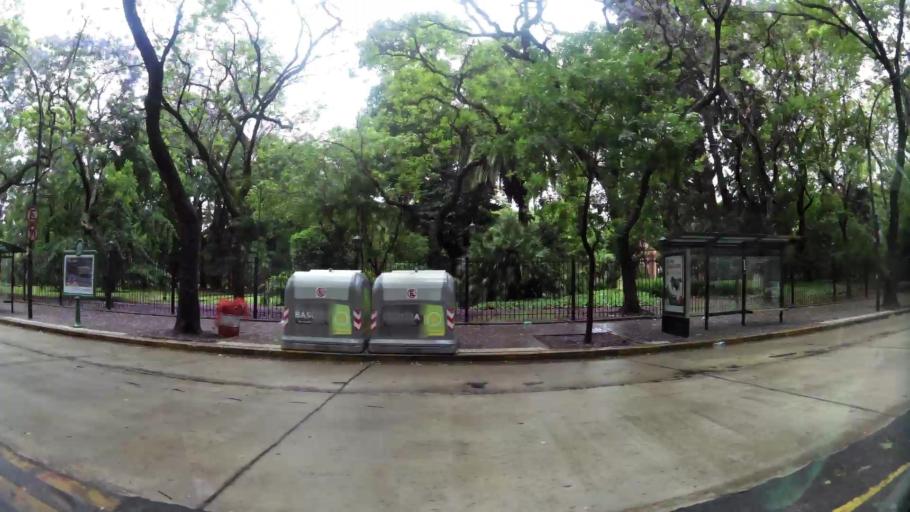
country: AR
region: Buenos Aires F.D.
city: Colegiales
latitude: -34.5827
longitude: -58.4195
